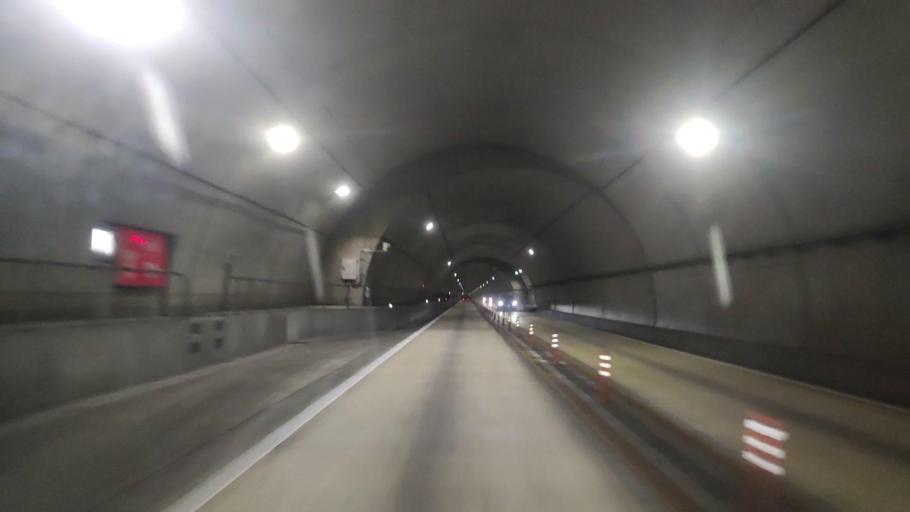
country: JP
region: Wakayama
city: Tanabe
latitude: 33.5693
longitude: 135.4862
